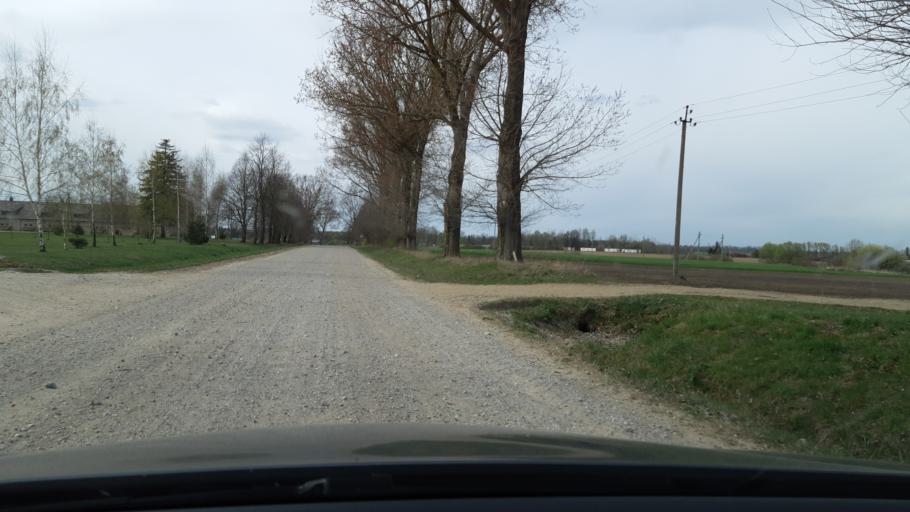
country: LT
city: Virbalis
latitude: 54.6193
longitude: 22.8393
